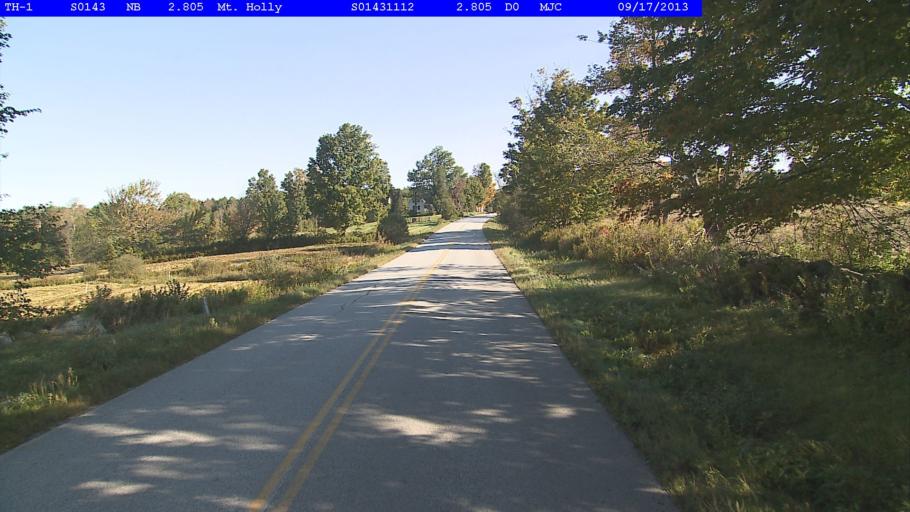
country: US
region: Vermont
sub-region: Rutland County
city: Rutland
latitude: 43.4379
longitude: -72.8271
